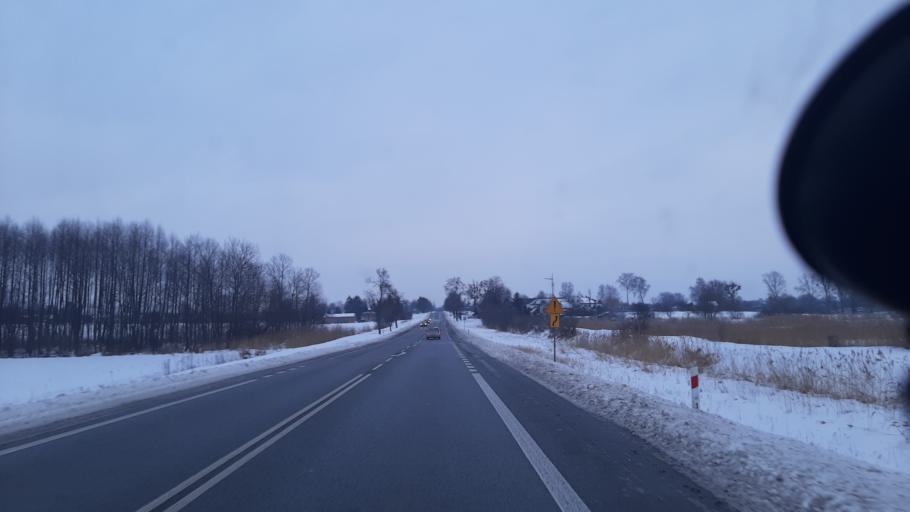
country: PL
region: Lublin Voivodeship
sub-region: Powiat lubelski
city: Garbow
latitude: 51.3613
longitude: 22.3083
